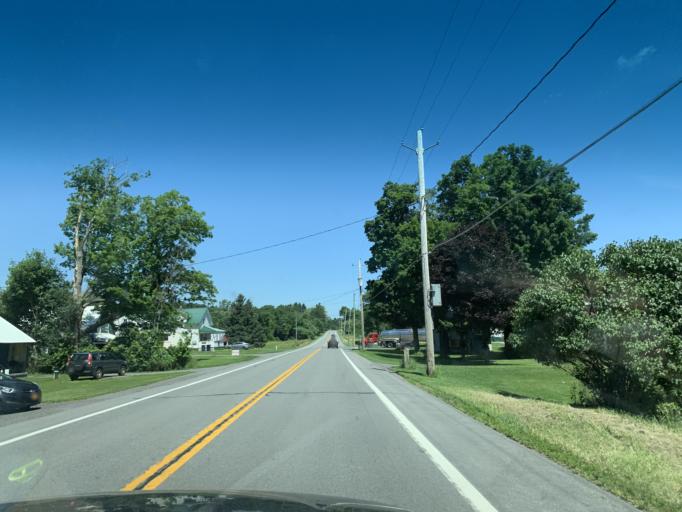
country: US
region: New York
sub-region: Oneida County
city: Chadwicks
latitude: 42.9231
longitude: -75.2465
